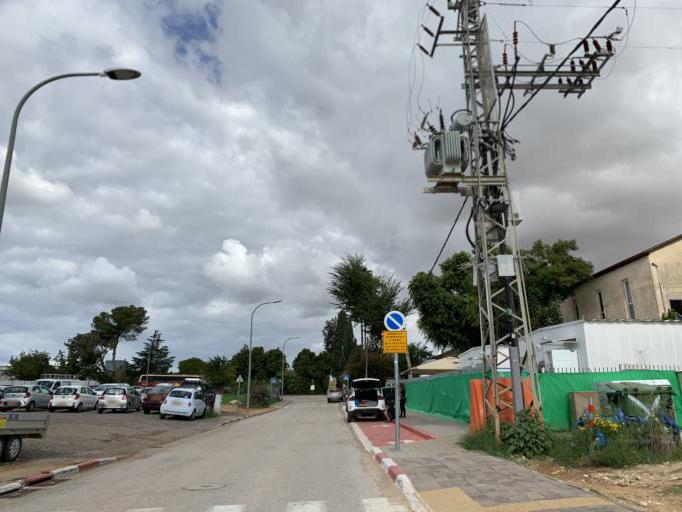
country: IL
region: Central District
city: Hod HaSharon
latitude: 32.1620
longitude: 34.8962
